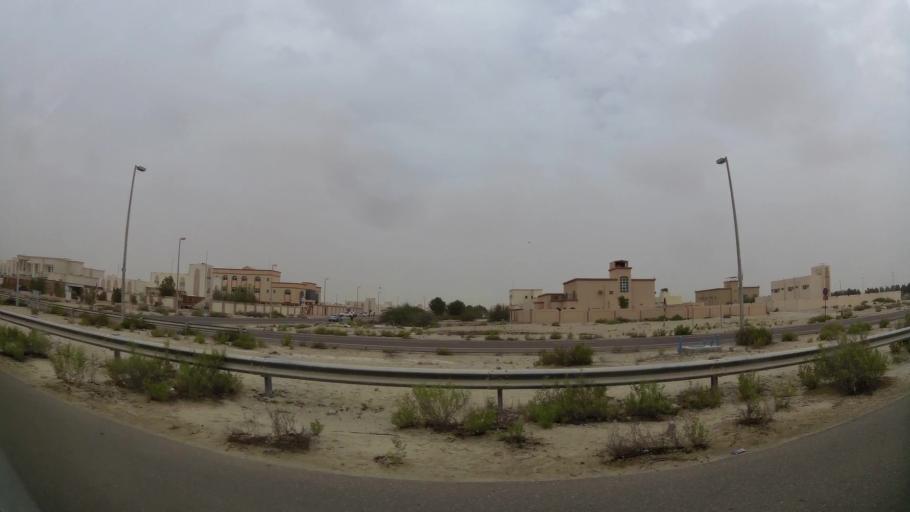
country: AE
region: Abu Dhabi
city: Abu Dhabi
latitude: 24.3912
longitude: 54.7159
